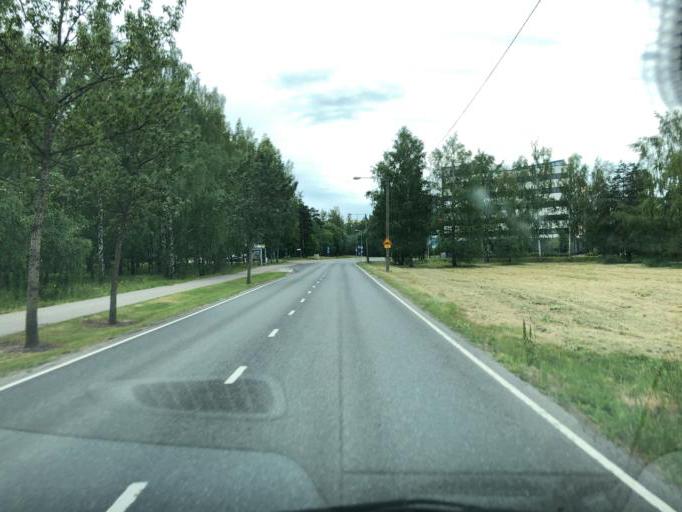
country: FI
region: Uusimaa
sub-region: Helsinki
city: Vantaa
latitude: 60.2950
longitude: 24.9722
